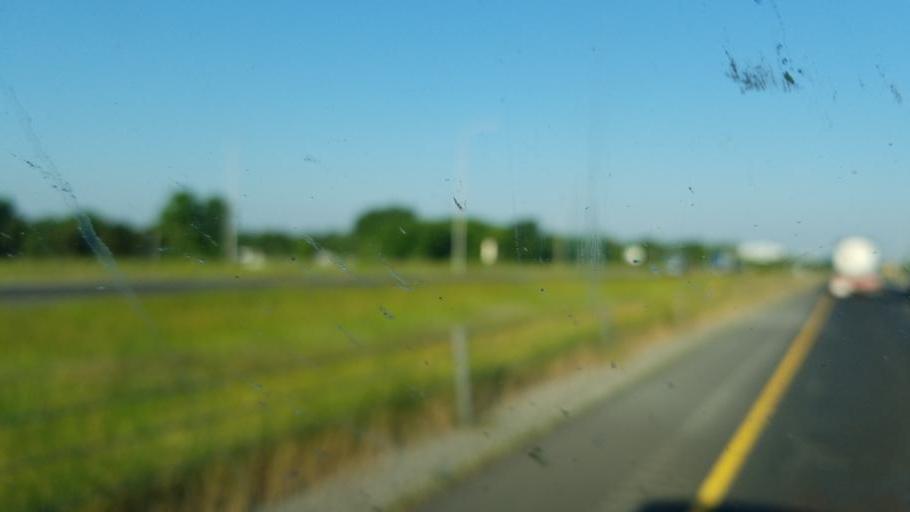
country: US
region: Illinois
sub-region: Will County
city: Shorewood
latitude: 41.4863
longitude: -88.2010
